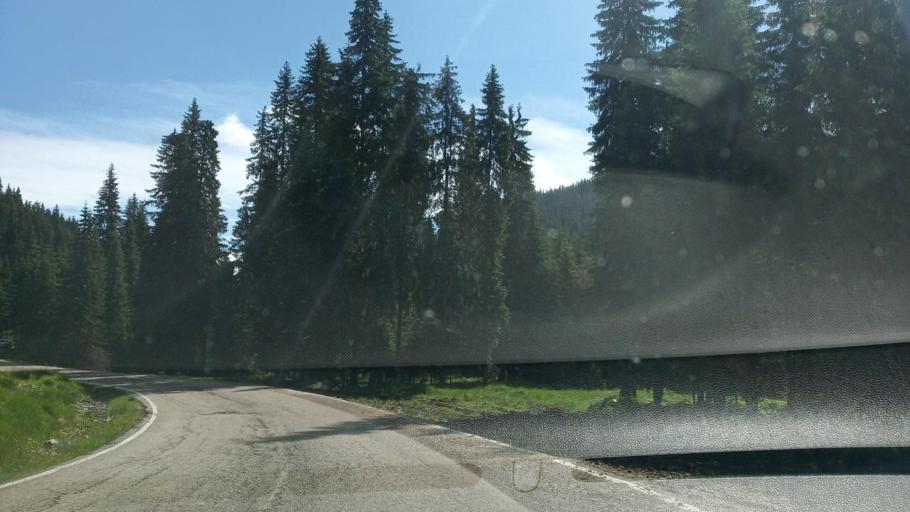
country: RO
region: Hunedoara
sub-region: Oras Petrila
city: Petrila
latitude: 45.4142
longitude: 23.6044
